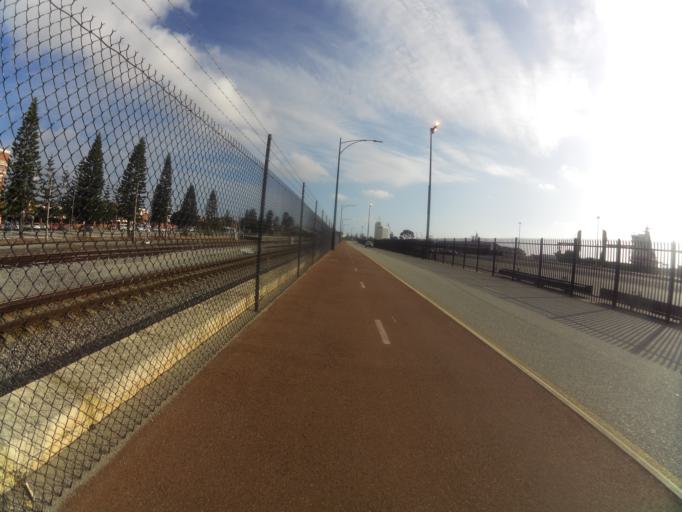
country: AU
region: Western Australia
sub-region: Fremantle
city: North Fremantle
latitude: -32.0498
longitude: 115.7469
